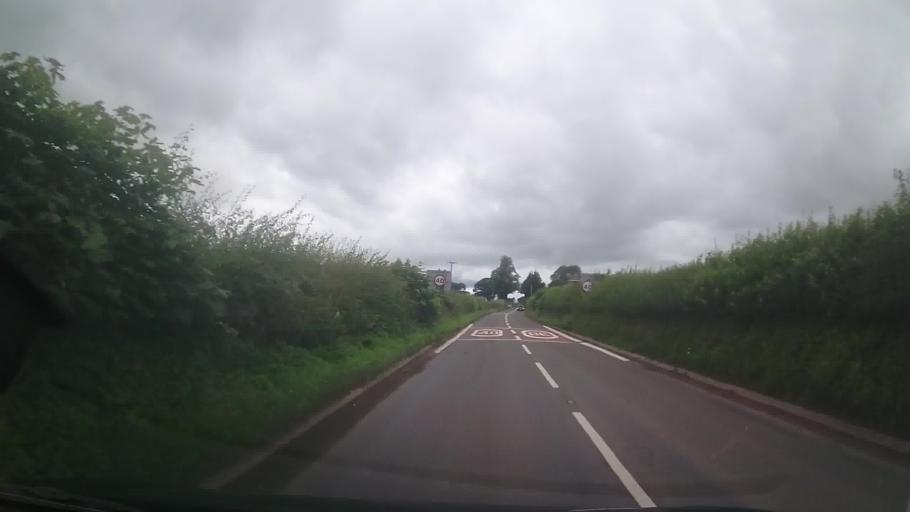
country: GB
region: England
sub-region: Shropshire
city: Petton
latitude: 52.8589
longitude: -2.8446
